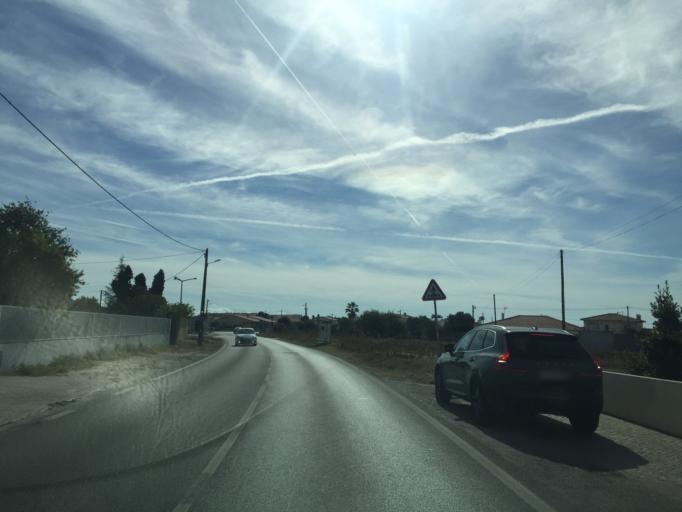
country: PT
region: Coimbra
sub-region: Figueira da Foz
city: Lavos
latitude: 40.0711
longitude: -8.8174
